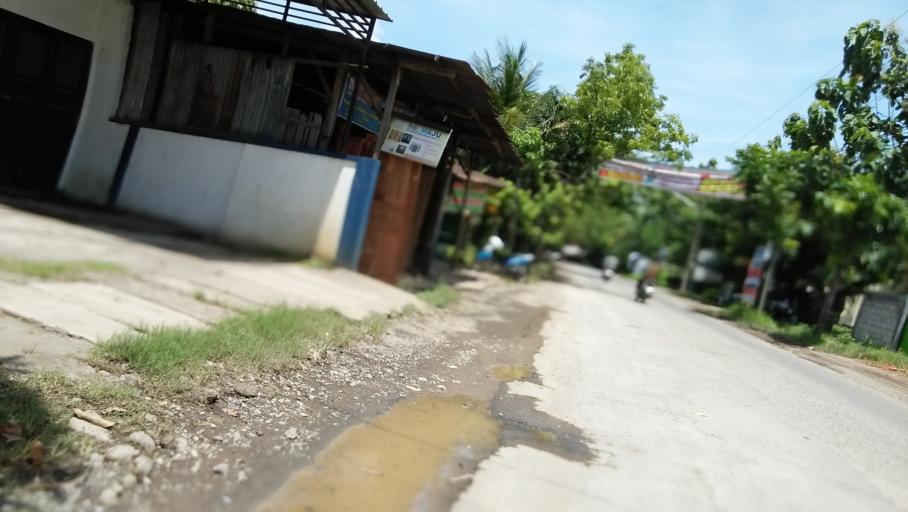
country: ID
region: Central Java
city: Mranggen
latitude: -7.0520
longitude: 110.4716
